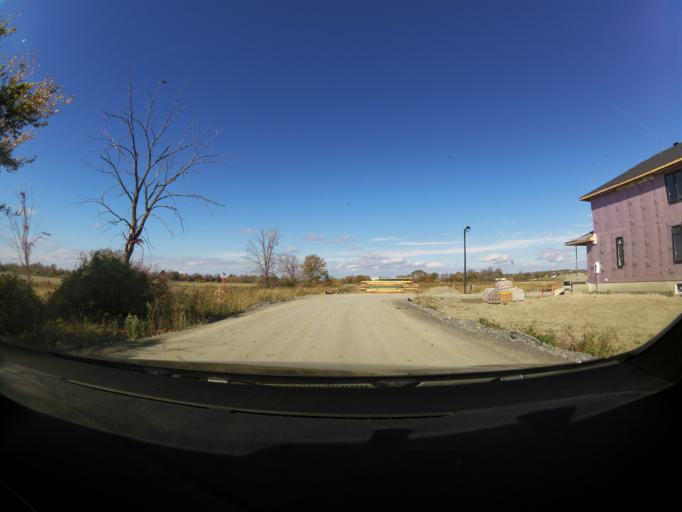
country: CA
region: Ontario
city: Bells Corners
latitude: 45.2807
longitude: -75.8964
